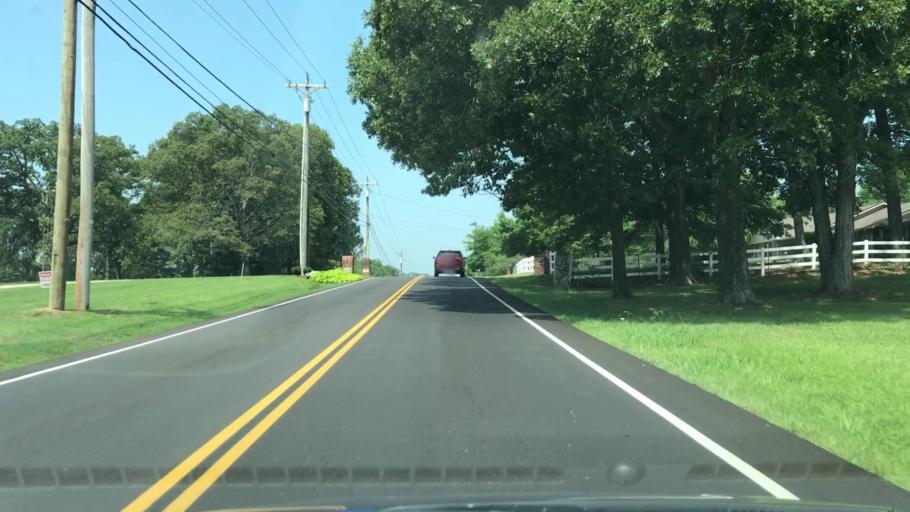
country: US
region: Tennessee
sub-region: Wilson County
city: Rural Hill
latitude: 36.1171
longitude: -86.4821
